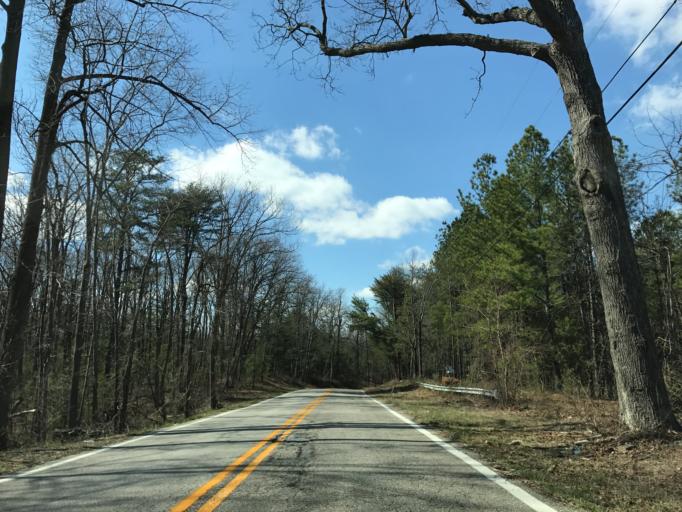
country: US
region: Maryland
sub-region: Anne Arundel County
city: Pasadena
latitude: 39.1305
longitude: -76.5789
